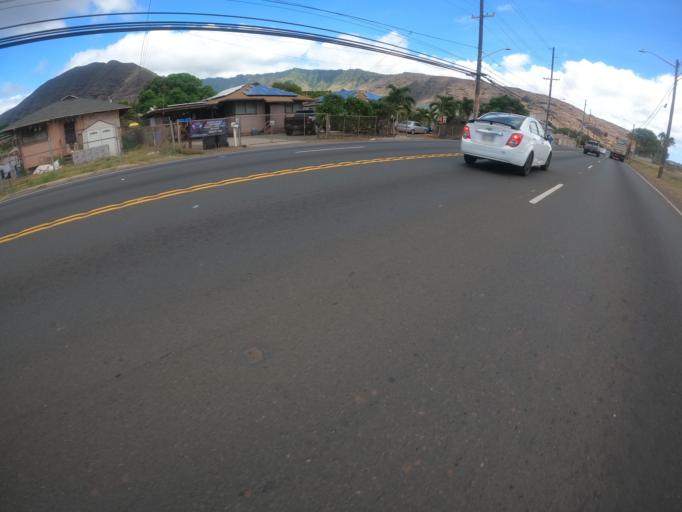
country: US
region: Hawaii
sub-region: Honolulu County
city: Nanakuli
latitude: 21.3851
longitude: -158.1495
